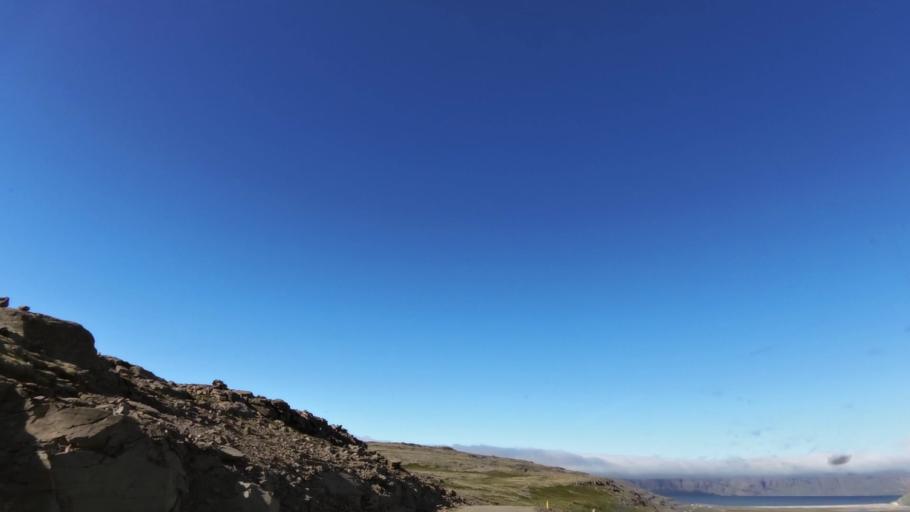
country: IS
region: West
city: Olafsvik
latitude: 65.5517
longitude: -24.2039
